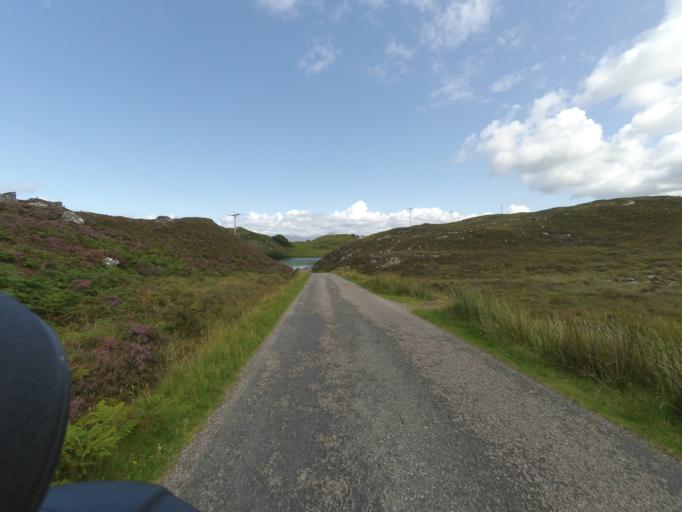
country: GB
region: Scotland
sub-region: Highland
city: Ullapool
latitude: 58.2418
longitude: -5.1938
